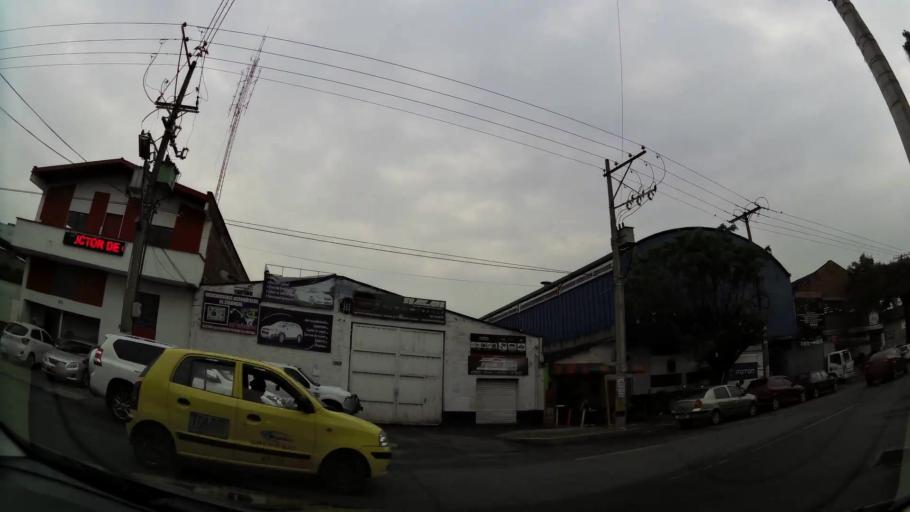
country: CO
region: Antioquia
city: Medellin
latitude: 6.2262
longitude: -75.5724
